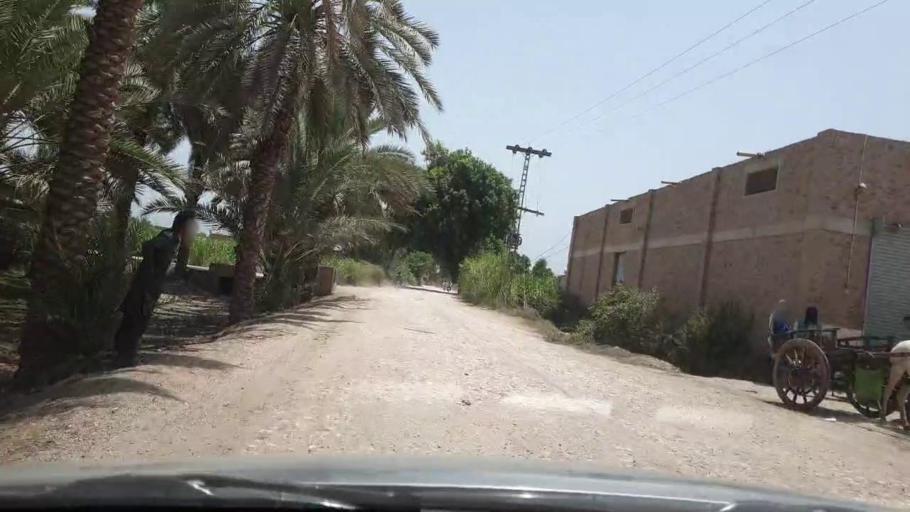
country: PK
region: Sindh
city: Pano Aqil
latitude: 27.8581
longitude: 69.0972
